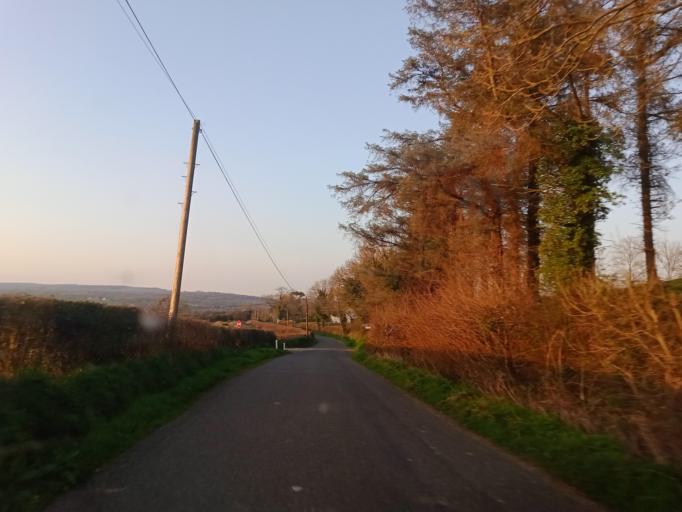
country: IE
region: Leinster
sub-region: Kilkenny
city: Castlecomer
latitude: 52.7377
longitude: -7.2375
